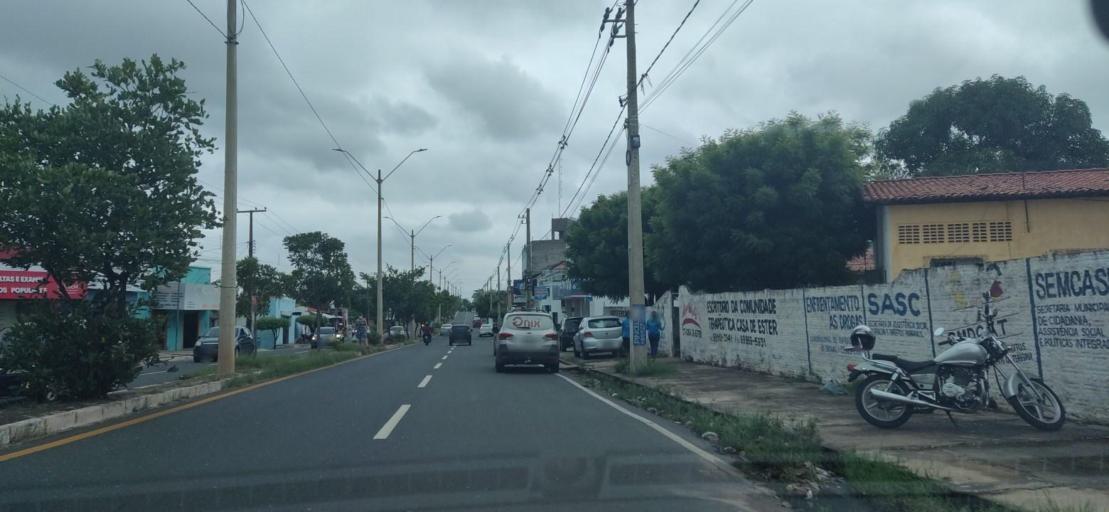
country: BR
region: Piaui
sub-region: Teresina
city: Teresina
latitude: -5.0536
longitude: -42.7446
